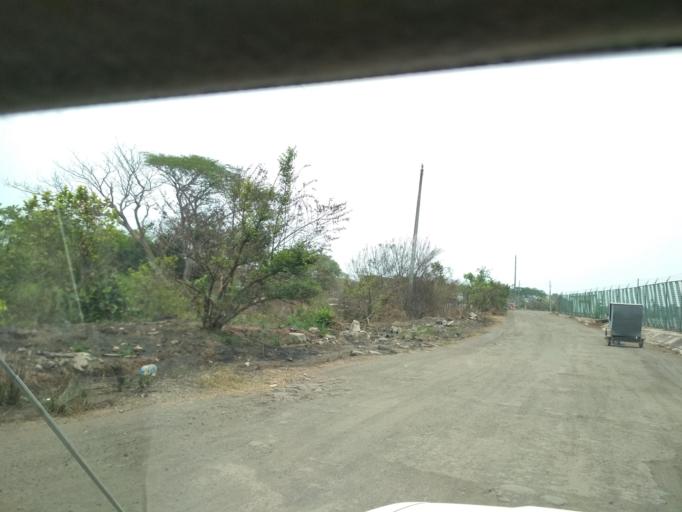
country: MX
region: Veracruz
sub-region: Veracruz
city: Delfino Victoria (Santa Fe)
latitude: 19.2006
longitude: -96.2642
